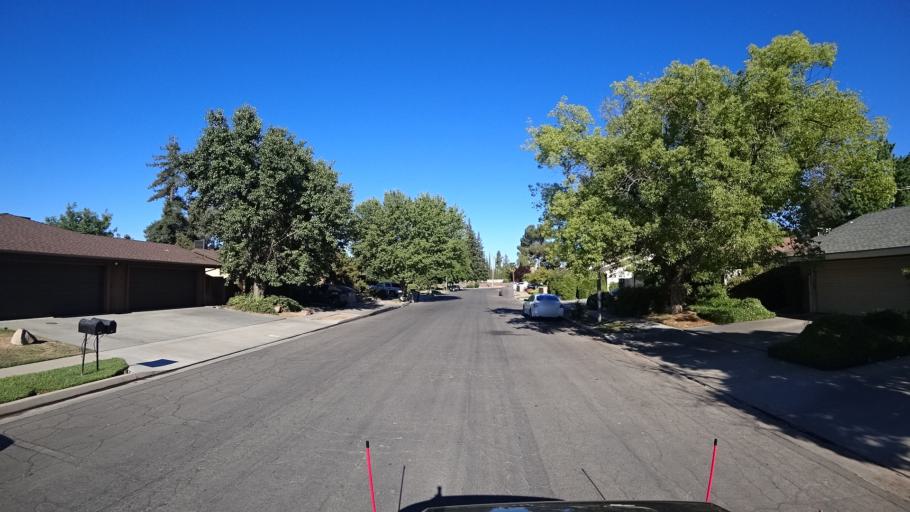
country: US
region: California
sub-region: Fresno County
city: Fresno
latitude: 36.8007
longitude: -119.8278
